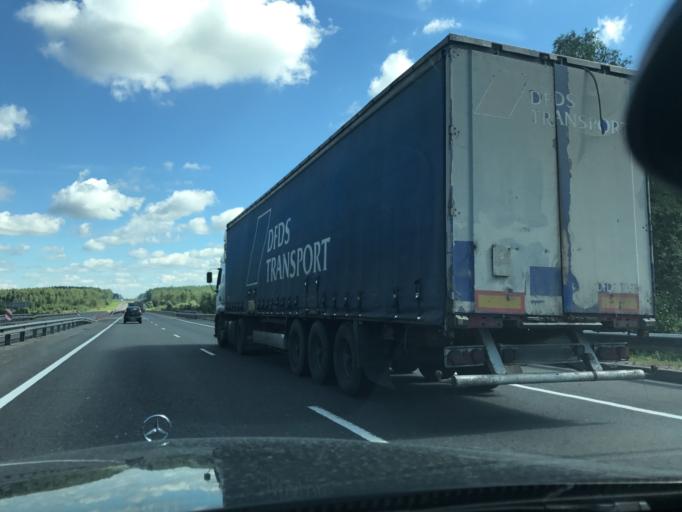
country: RU
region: Vladimir
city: Sudogda
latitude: 56.1230
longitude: 40.8613
